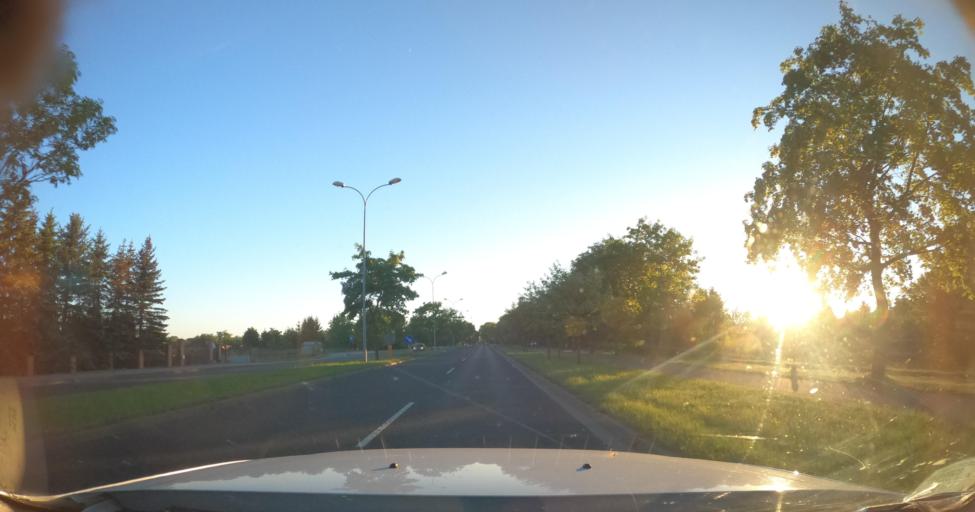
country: PL
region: Pomeranian Voivodeship
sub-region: Slupsk
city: Slupsk
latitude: 54.4699
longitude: 17.0710
